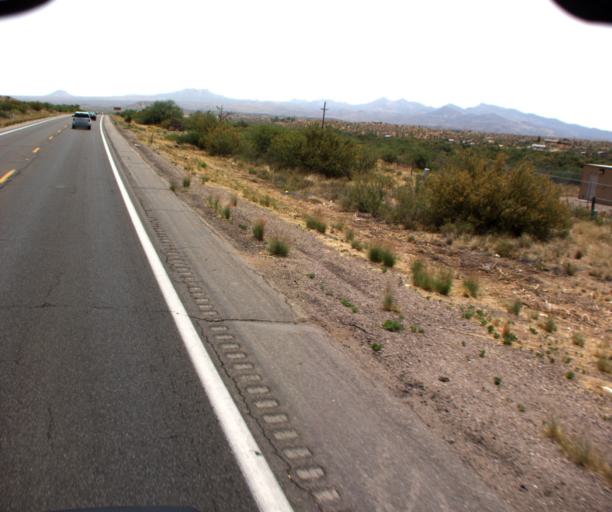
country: US
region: Arizona
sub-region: Gila County
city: Globe
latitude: 33.3669
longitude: -110.7179
